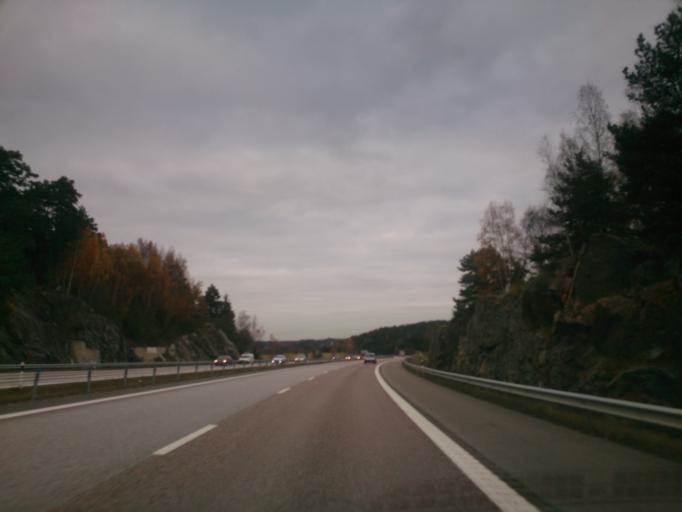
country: SE
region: Soedermanland
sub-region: Gnesta Kommun
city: Gnesta
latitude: 58.8756
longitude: 17.2319
